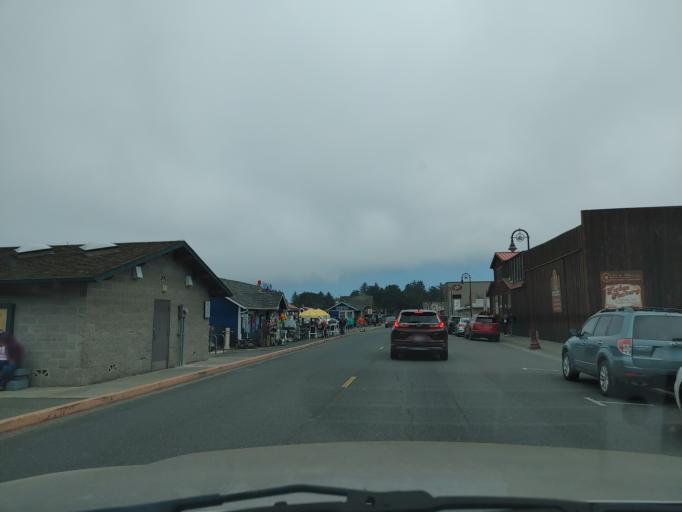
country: US
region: Oregon
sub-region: Coos County
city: Bandon
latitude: 43.1198
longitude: -124.4143
